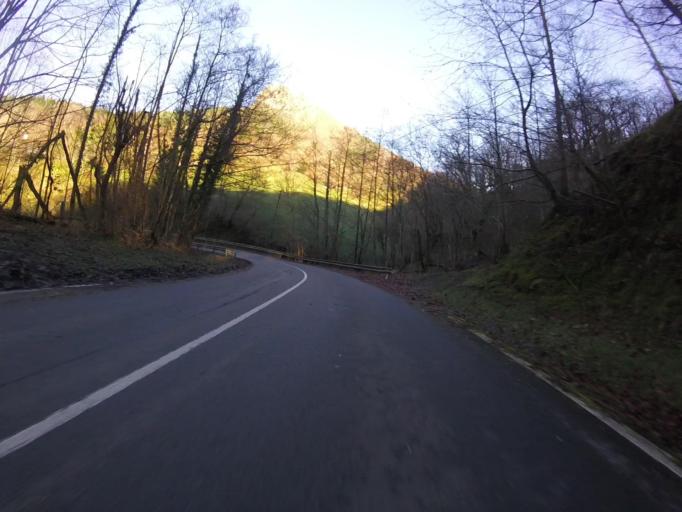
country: ES
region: Basque Country
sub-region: Provincia de Guipuzcoa
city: Irun
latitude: 43.2738
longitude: -1.7681
